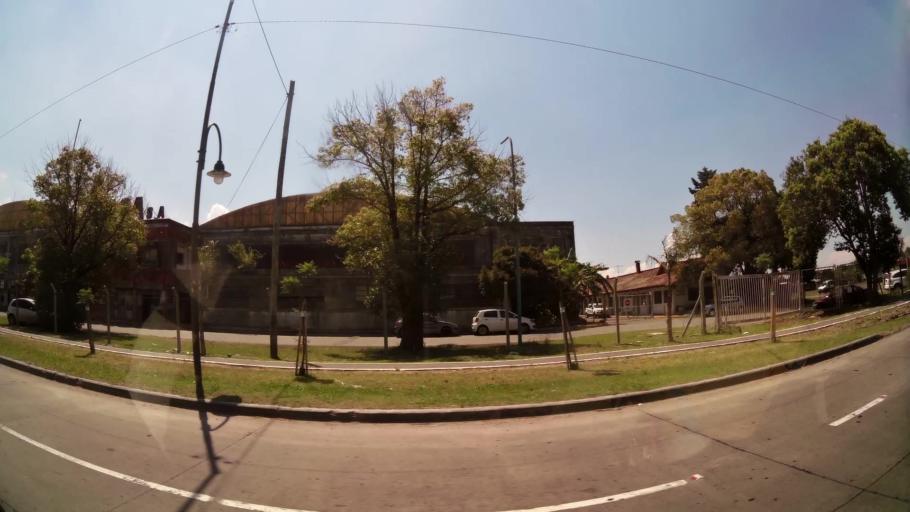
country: AR
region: Buenos Aires
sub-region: Partido de Tigre
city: Tigre
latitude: -34.4543
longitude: -58.5788
